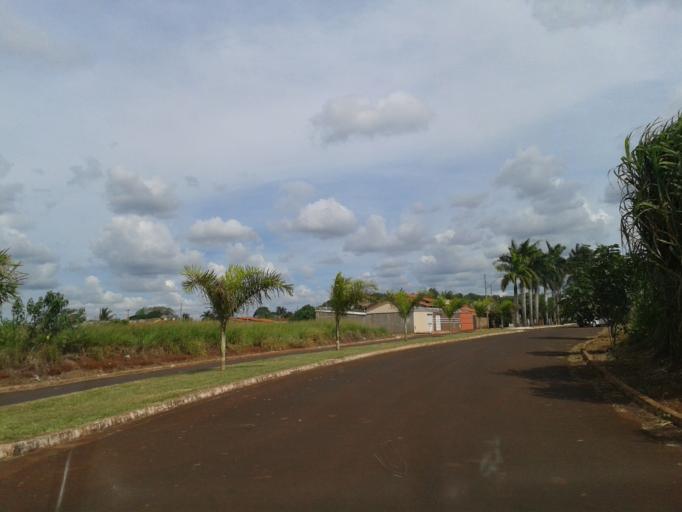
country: BR
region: Minas Gerais
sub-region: Centralina
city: Centralina
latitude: -18.5792
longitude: -49.1957
